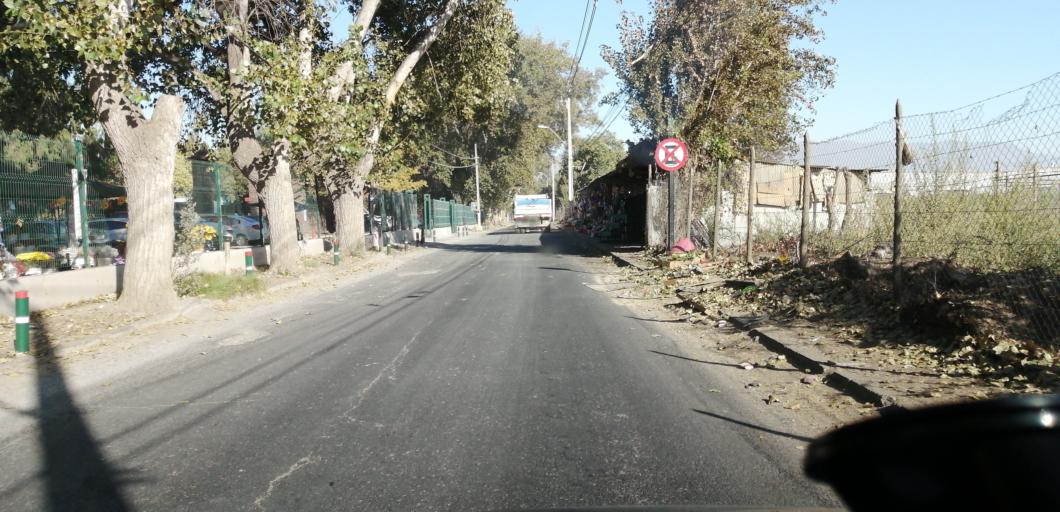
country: CL
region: Santiago Metropolitan
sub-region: Provincia de Santiago
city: Lo Prado
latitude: -33.4633
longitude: -70.7661
